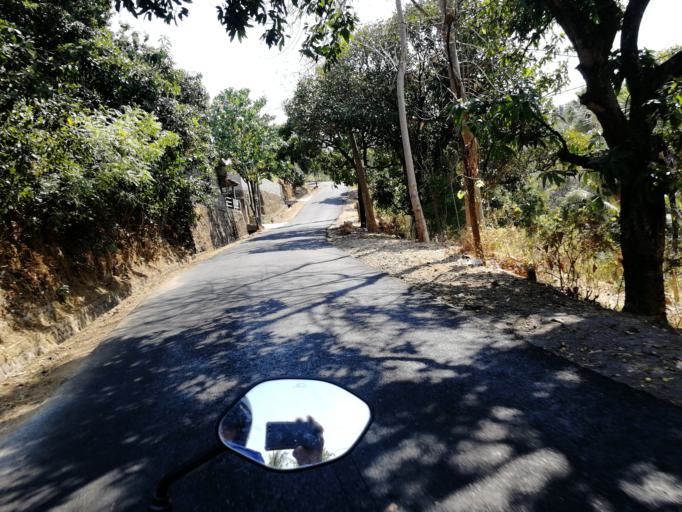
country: ID
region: Bali
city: Banjar Trunyan
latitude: -8.1297
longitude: 115.3244
